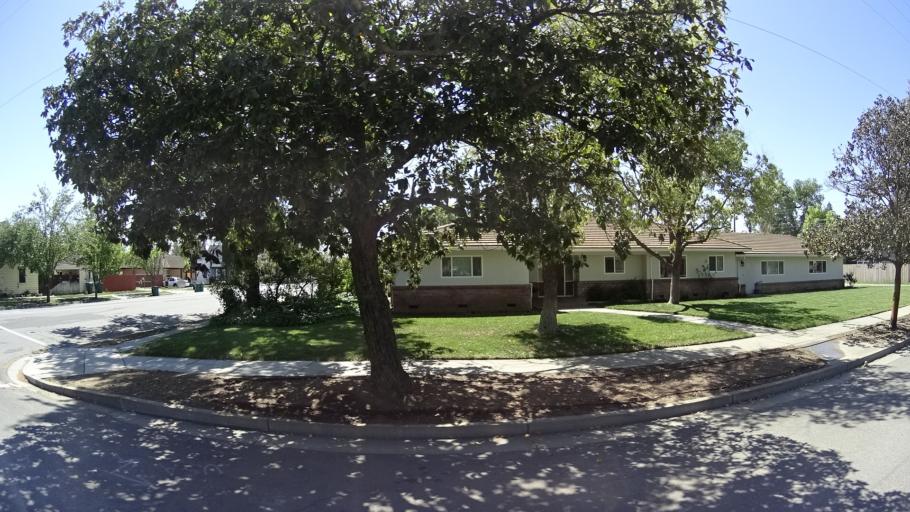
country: US
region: California
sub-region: Glenn County
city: Willows
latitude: 39.5179
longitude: -122.2000
